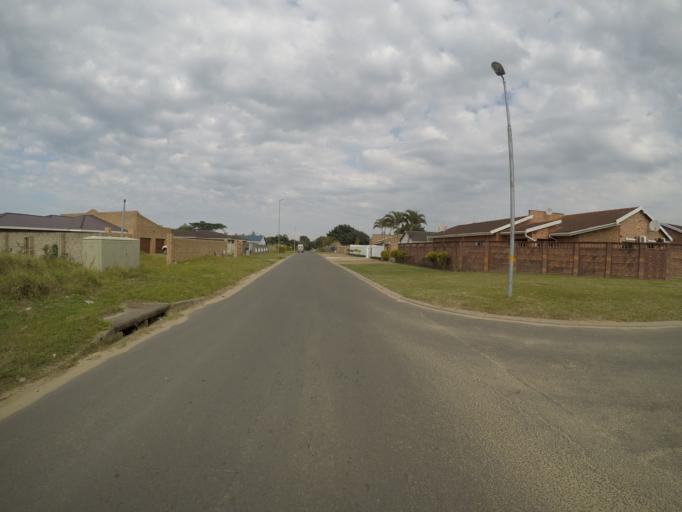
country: ZA
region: KwaZulu-Natal
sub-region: uThungulu District Municipality
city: Richards Bay
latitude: -28.7343
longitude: 32.0860
